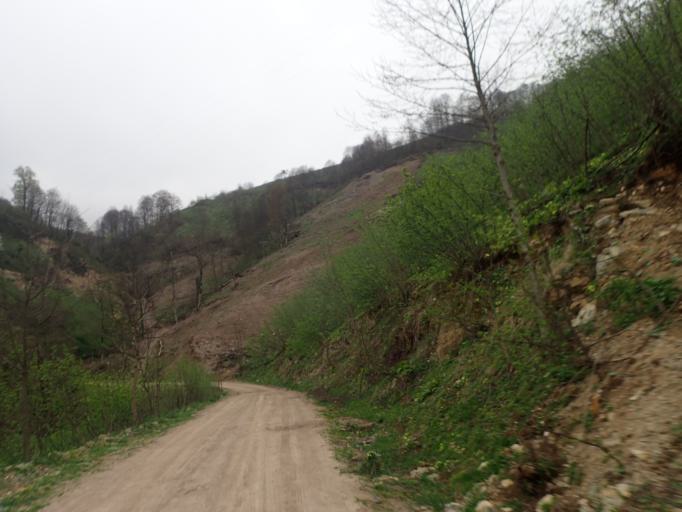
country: TR
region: Ordu
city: Korgan
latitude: 40.7756
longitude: 37.3483
